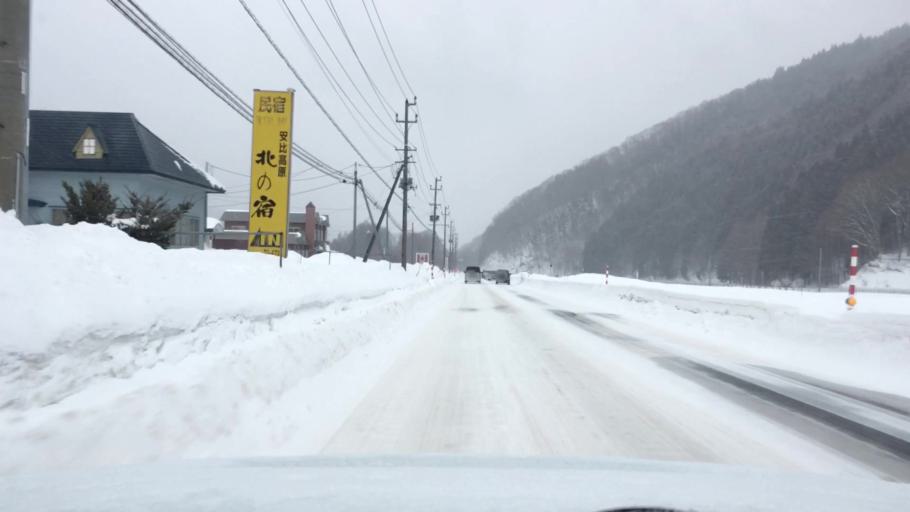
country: JP
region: Akita
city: Hanawa
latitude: 40.0376
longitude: 140.9935
